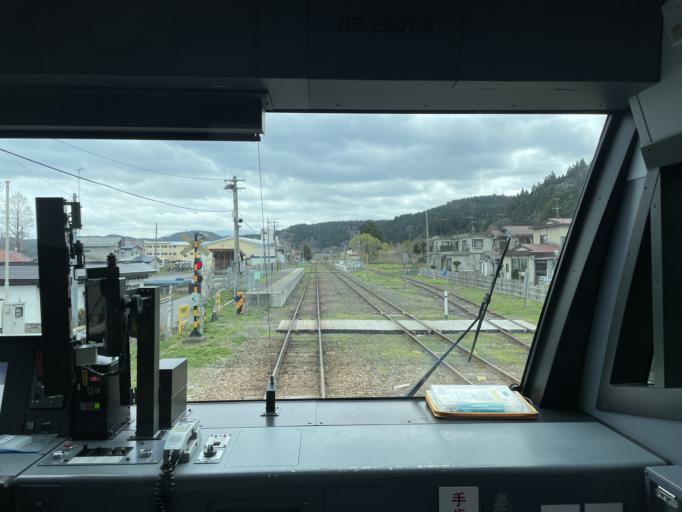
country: JP
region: Aomori
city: Shimokizukuri
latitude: 40.7465
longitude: 140.0944
